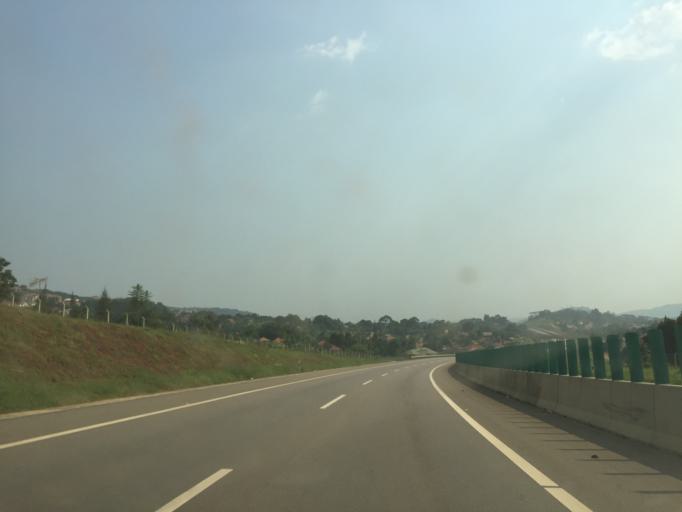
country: UG
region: Central Region
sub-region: Wakiso District
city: Kajansi
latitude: 0.2577
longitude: 32.5224
